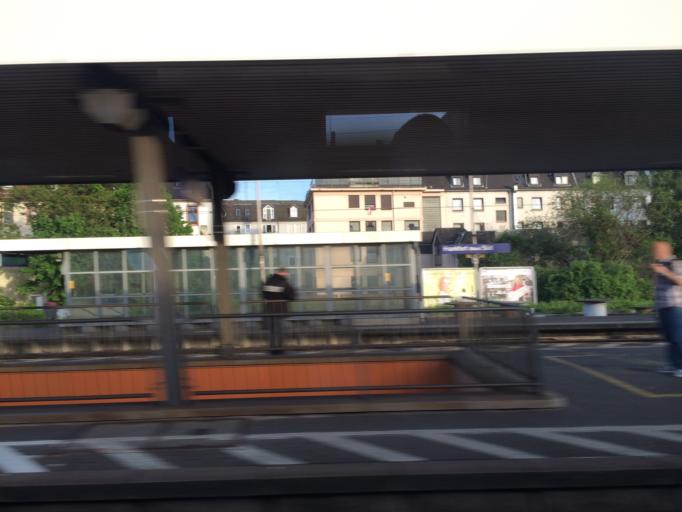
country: DE
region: Hesse
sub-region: Regierungsbezirk Darmstadt
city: Frankfurt am Main
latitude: 50.0993
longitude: 8.6867
